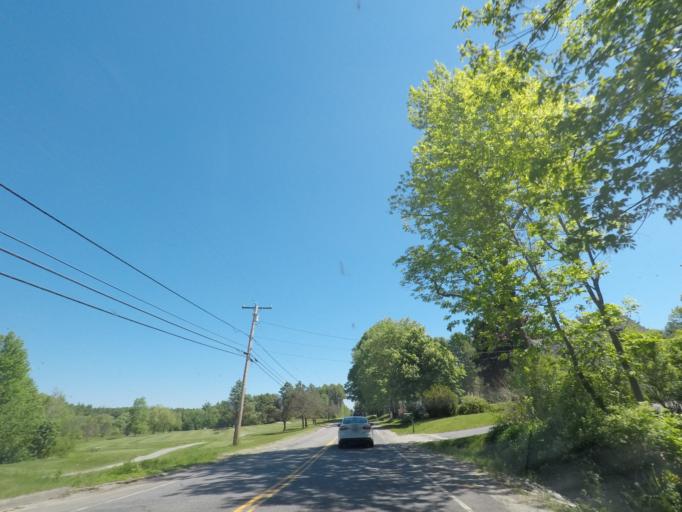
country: US
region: Maine
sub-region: Kennebec County
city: Manchester
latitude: 44.3167
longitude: -69.8701
